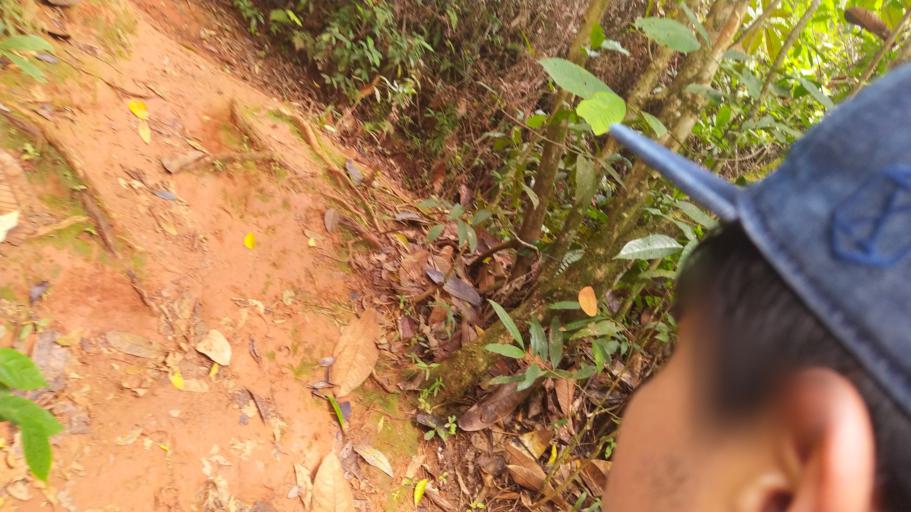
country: CO
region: Valle del Cauca
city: Cali
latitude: 3.4226
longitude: -76.6150
